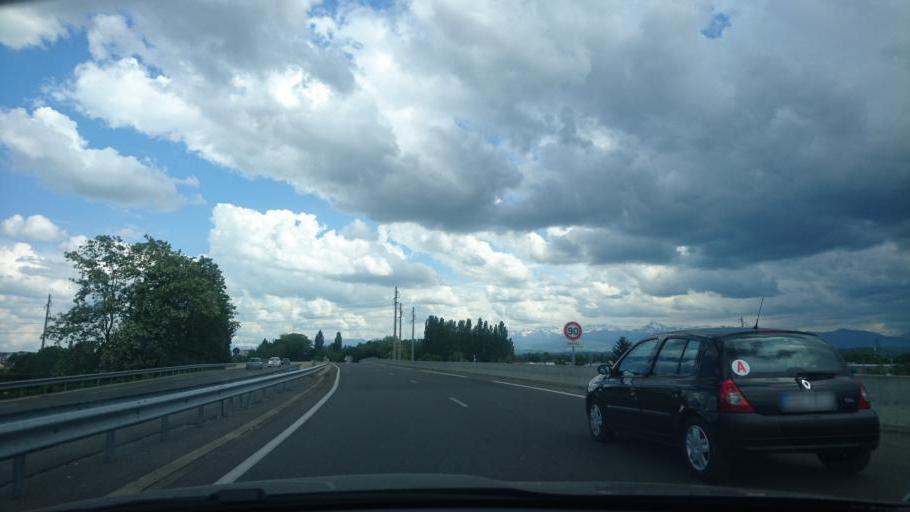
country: FR
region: Midi-Pyrenees
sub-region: Departement des Hautes-Pyrenees
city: Juillan
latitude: 43.2307
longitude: 0.0430
